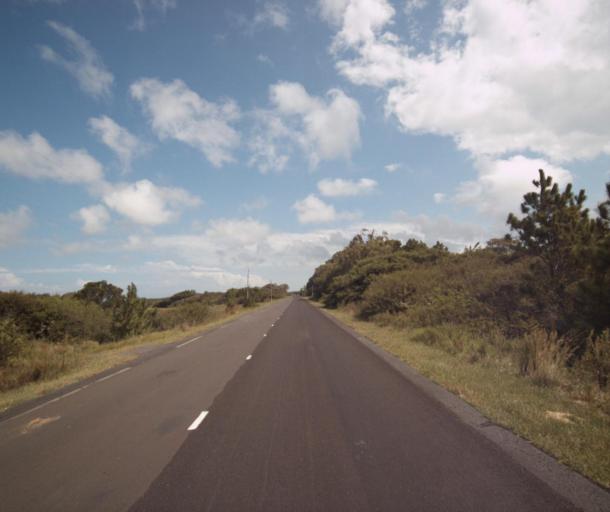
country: BR
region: Rio Grande do Sul
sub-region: Tapes
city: Tapes
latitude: -31.4026
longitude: -51.1647
